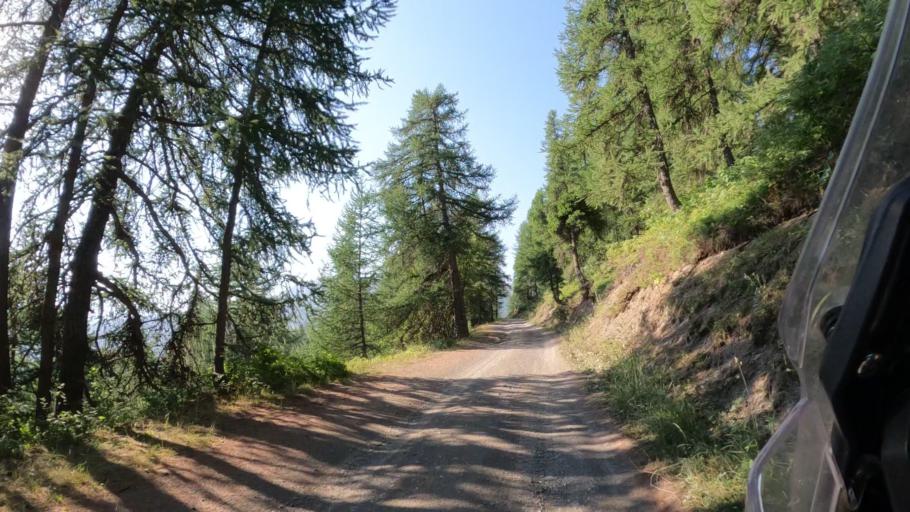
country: FR
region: Provence-Alpes-Cote d'Azur
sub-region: Departement des Hautes-Alpes
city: Guillestre
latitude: 44.6215
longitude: 6.6235
